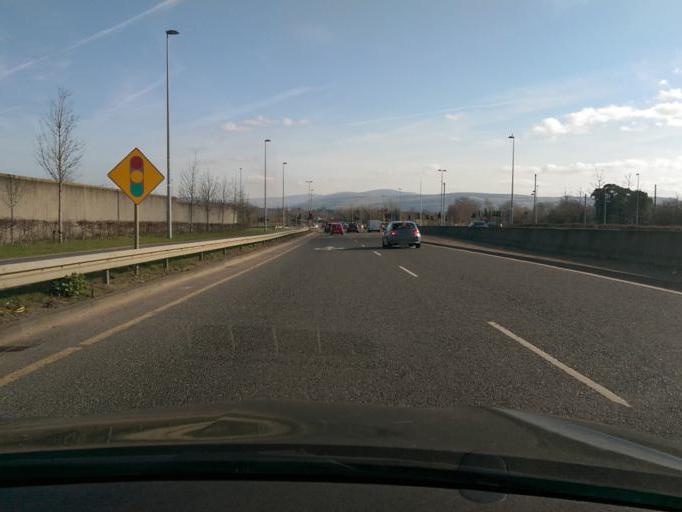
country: IE
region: Leinster
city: Clondalkin
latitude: 53.3207
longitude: -6.4300
